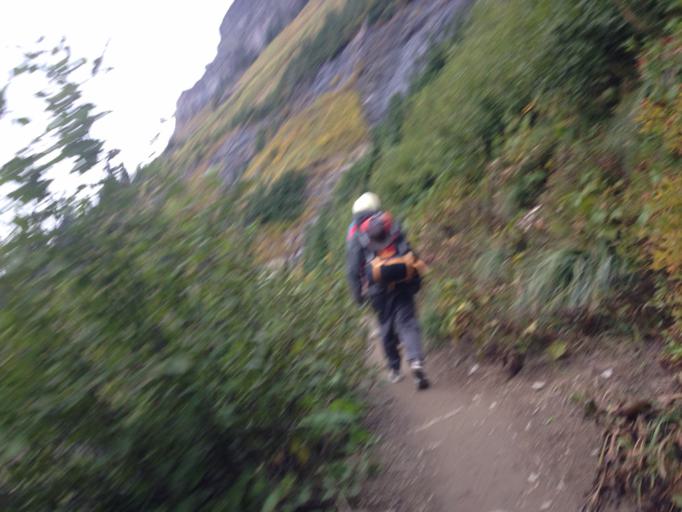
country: US
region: Montana
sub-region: Flathead County
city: Columbia Falls
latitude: 48.7196
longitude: -113.7190
